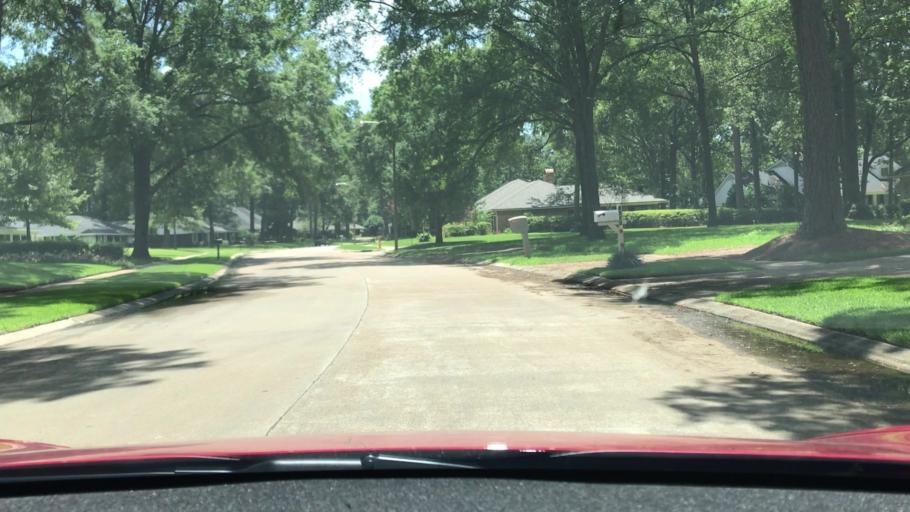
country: US
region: Louisiana
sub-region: Bossier Parish
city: Bossier City
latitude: 32.4293
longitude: -93.7374
